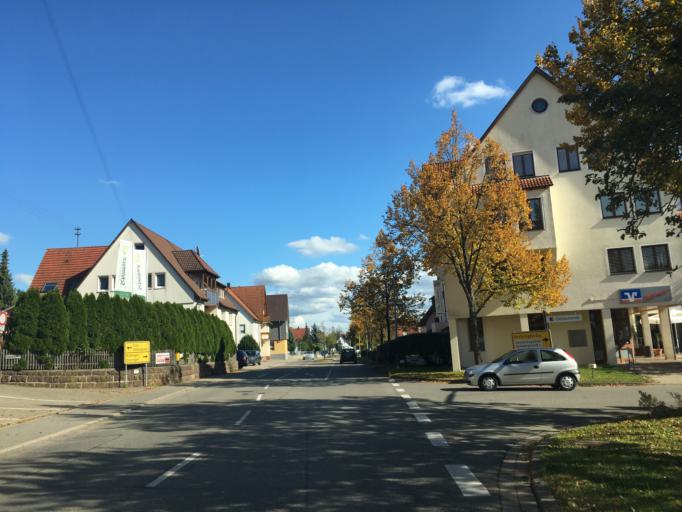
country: DE
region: Baden-Wuerttemberg
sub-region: Karlsruhe Region
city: Ostelsheim
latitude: 48.7275
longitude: 8.8495
